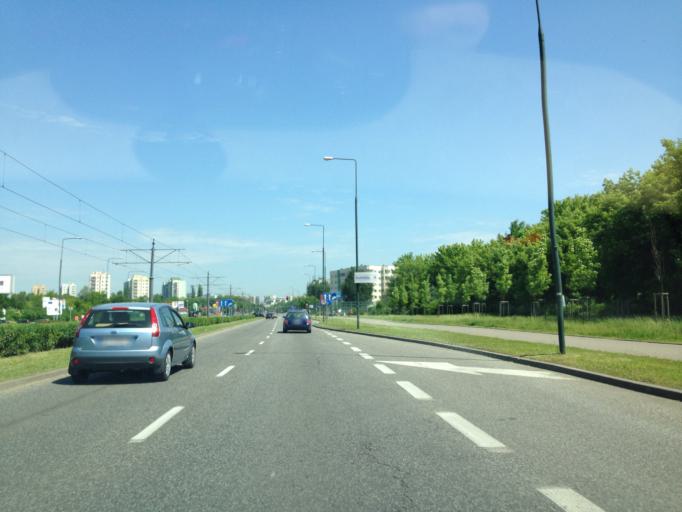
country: PL
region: Masovian Voivodeship
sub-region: Warszawa
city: Bielany
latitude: 52.2667
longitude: 20.9317
